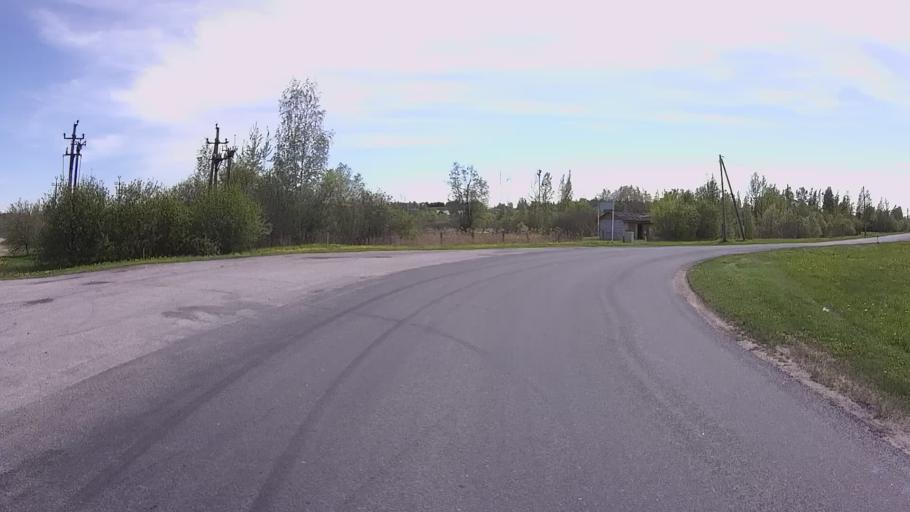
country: EE
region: Valgamaa
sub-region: Valga linn
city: Valga
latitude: 57.7747
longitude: 26.0734
